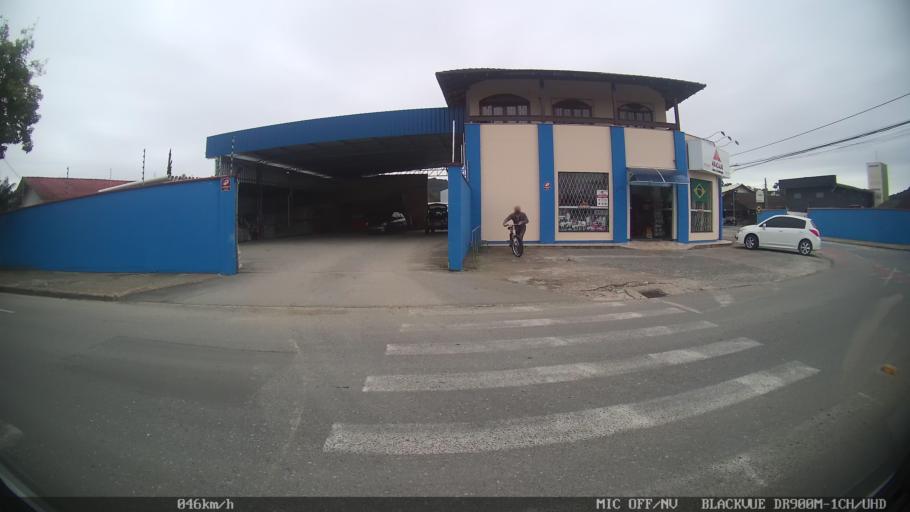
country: BR
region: Santa Catarina
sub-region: Joinville
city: Joinville
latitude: -26.2754
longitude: -48.8438
